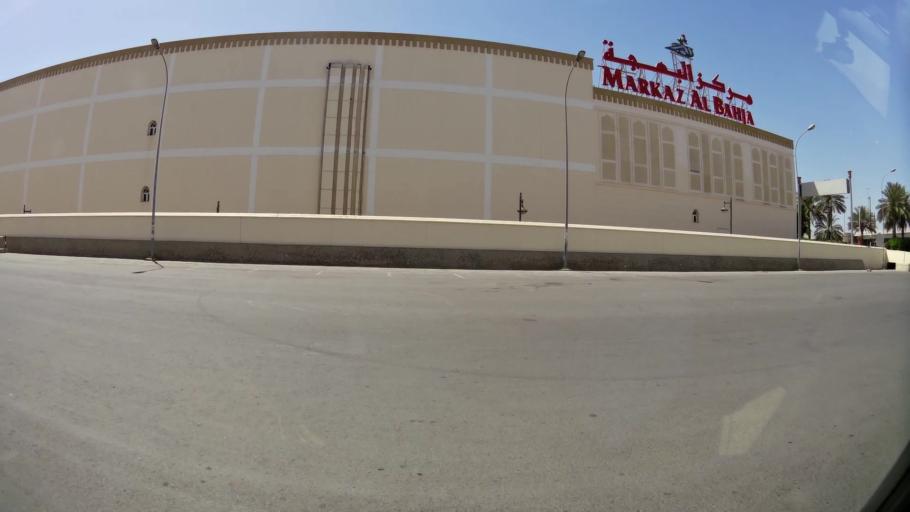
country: OM
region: Muhafazat Masqat
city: As Sib al Jadidah
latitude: 23.6144
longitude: 58.2460
